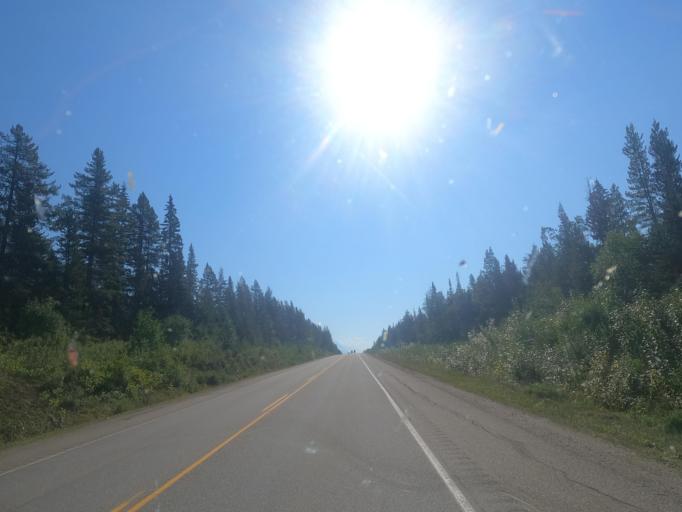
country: CA
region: Alberta
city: Jasper Park Lodge
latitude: 52.9778
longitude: -118.9689
